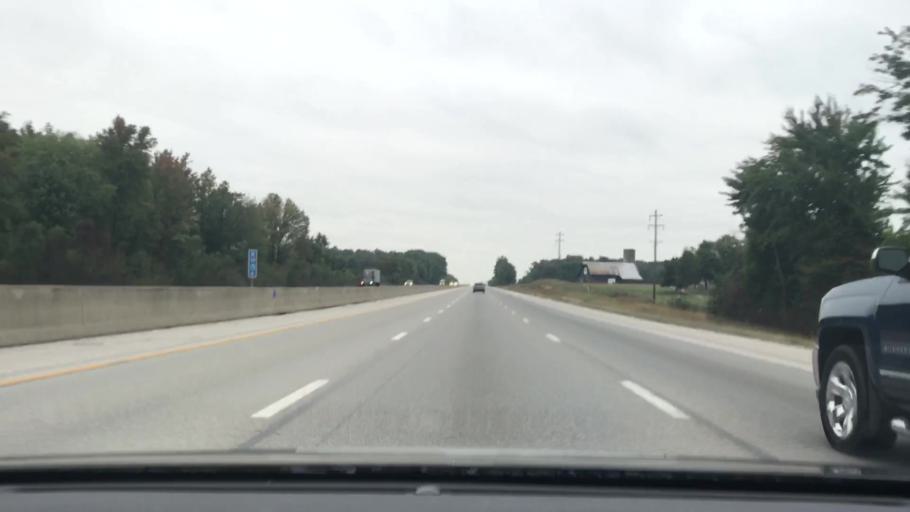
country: US
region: Kentucky
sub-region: Warren County
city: Plano
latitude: 36.8430
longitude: -86.4619
